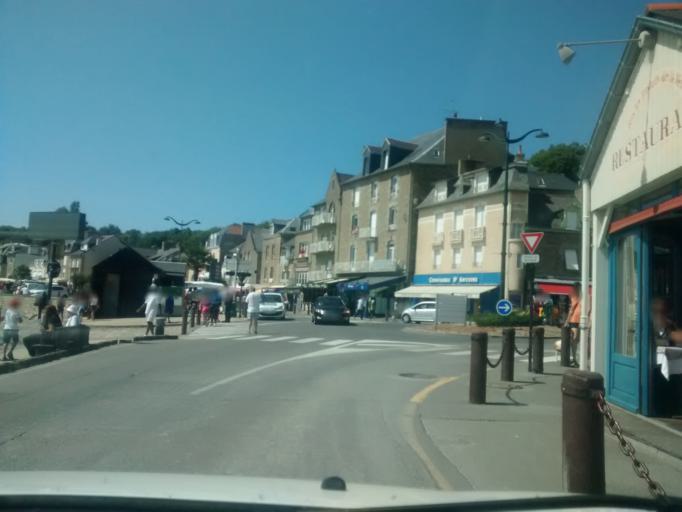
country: FR
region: Brittany
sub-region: Departement d'Ille-et-Vilaine
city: Cancale
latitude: 48.6710
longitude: -1.8527
